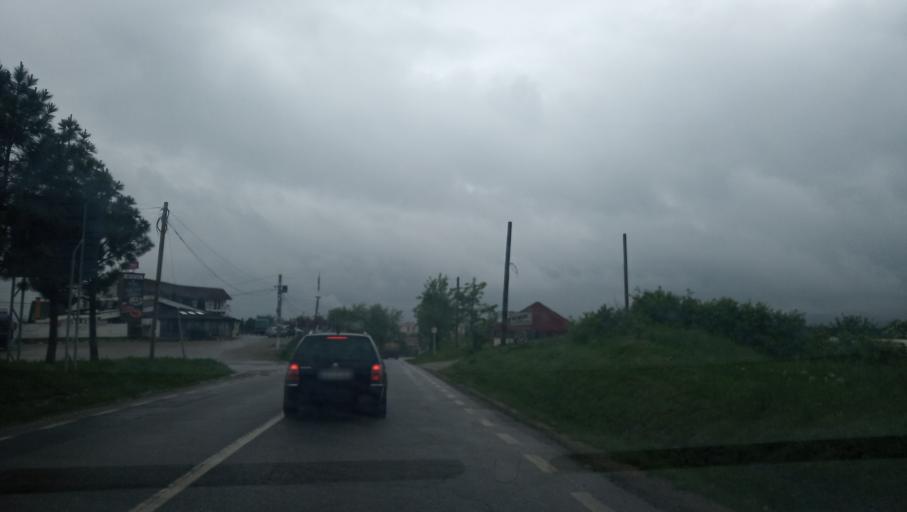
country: RO
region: Alba
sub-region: Municipiul Sebes
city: Sebes
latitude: 45.9484
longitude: 23.5854
